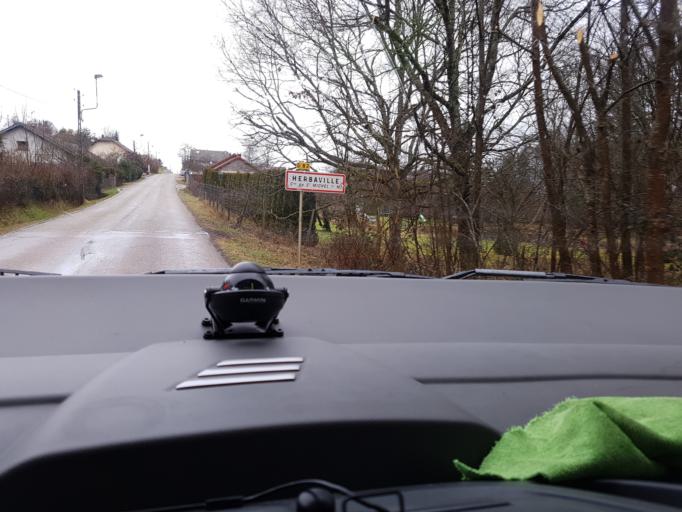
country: FR
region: Lorraine
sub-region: Departement des Vosges
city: Saint-Michel-sur-Meurthe
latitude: 48.3051
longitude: 6.9106
